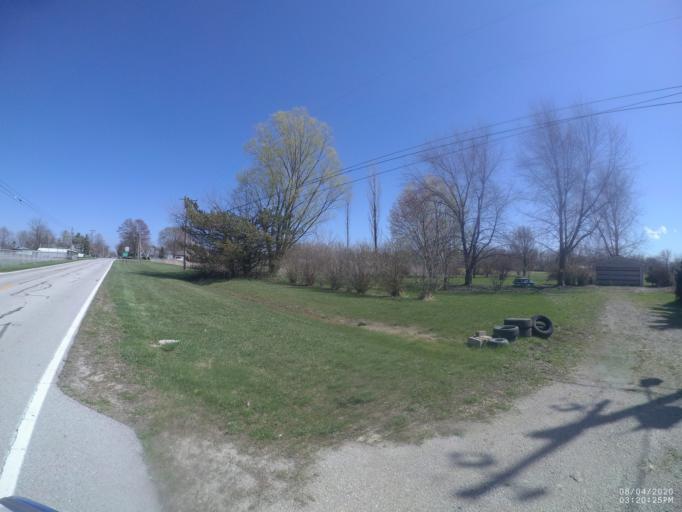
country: US
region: Ohio
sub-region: Sandusky County
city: Gibsonburg
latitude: 41.2677
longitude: -83.2583
